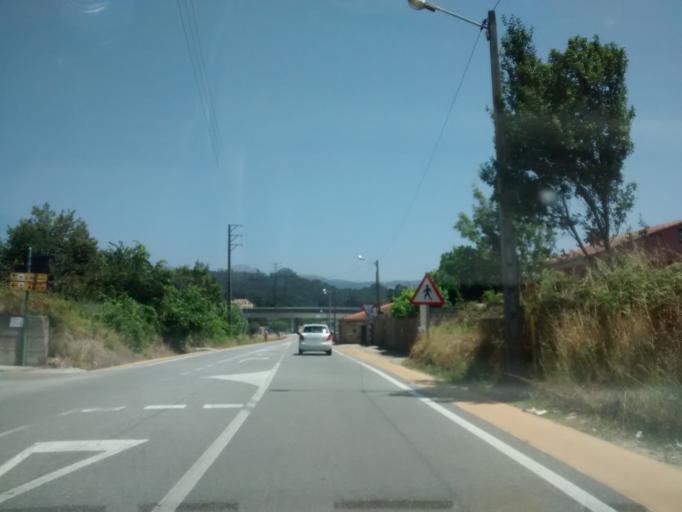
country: ES
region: Galicia
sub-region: Provincia de Pontevedra
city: Nigran
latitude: 42.1138
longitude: -8.7926
